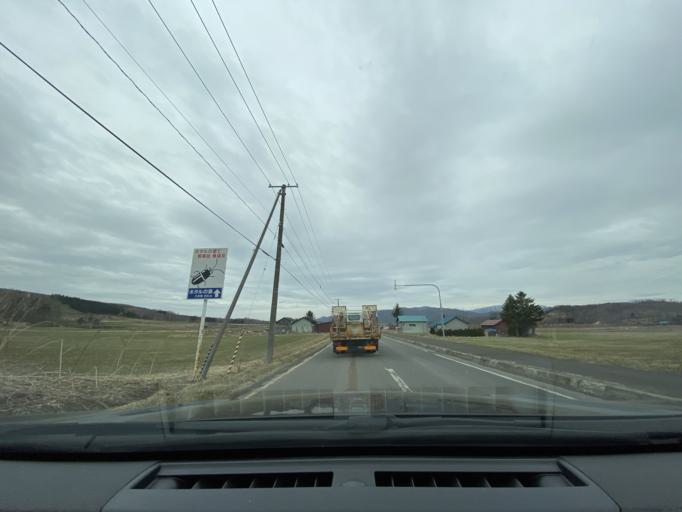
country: JP
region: Hokkaido
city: Nayoro
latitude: 44.0934
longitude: 142.4734
